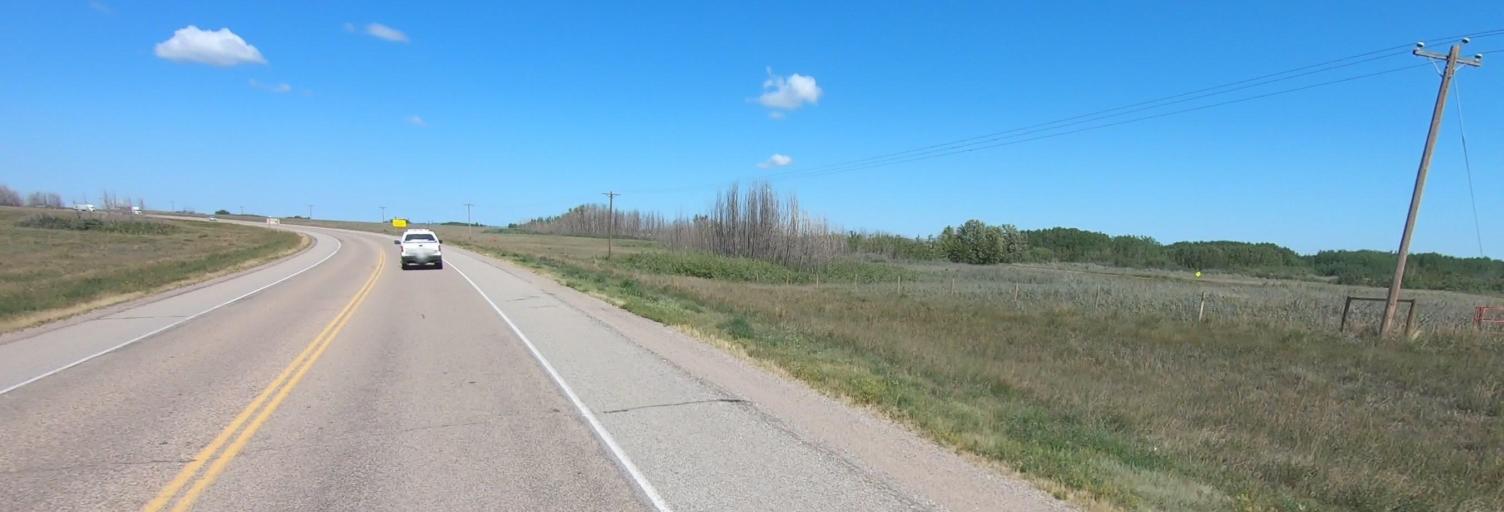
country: CA
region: Alberta
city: Strathmore
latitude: 50.8788
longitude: -113.1684
